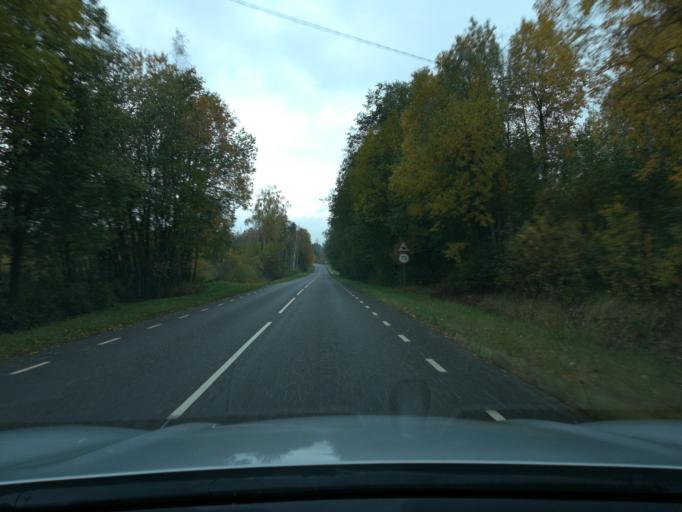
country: EE
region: Ida-Virumaa
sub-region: Johvi vald
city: Johvi
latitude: 59.0655
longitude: 27.3815
